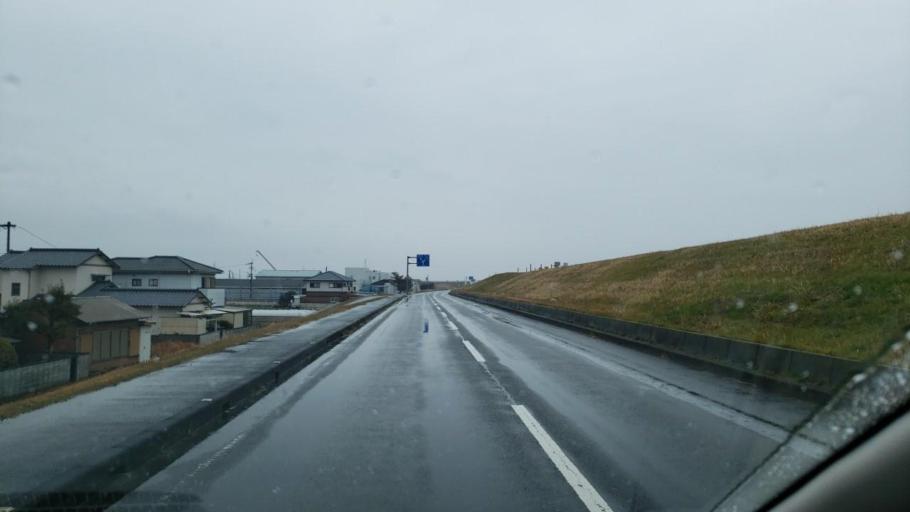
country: JP
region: Tokushima
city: Ishii
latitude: 34.1076
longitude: 134.4303
